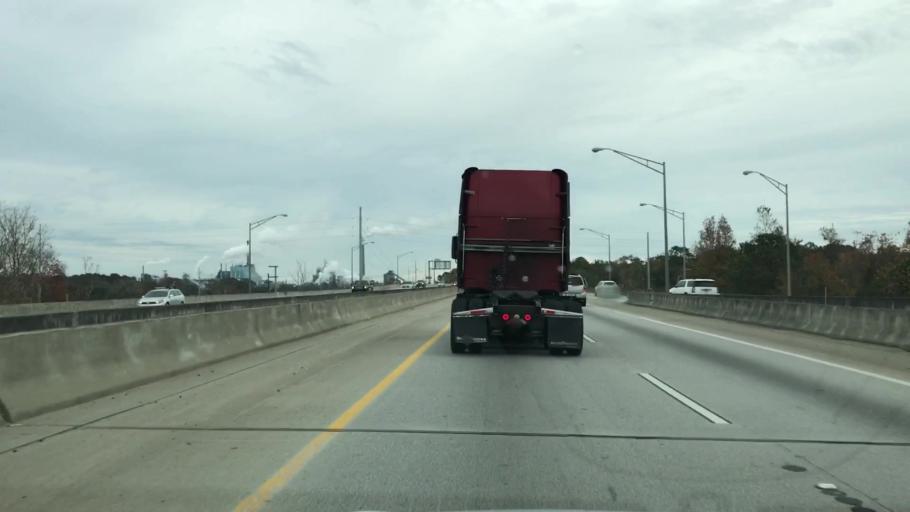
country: US
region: South Carolina
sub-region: Charleston County
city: North Charleston
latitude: 32.8942
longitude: -79.9881
